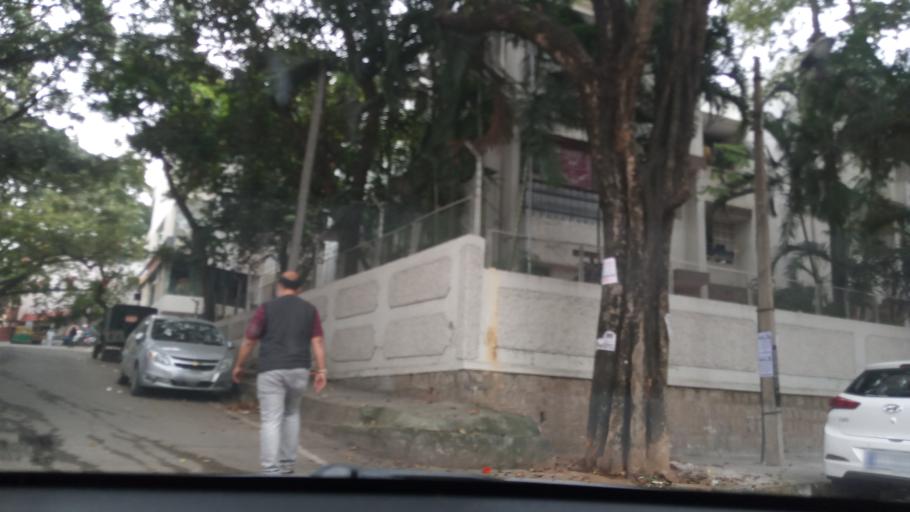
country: IN
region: Karnataka
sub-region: Bangalore Urban
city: Bangalore
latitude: 13.0104
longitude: 77.5383
